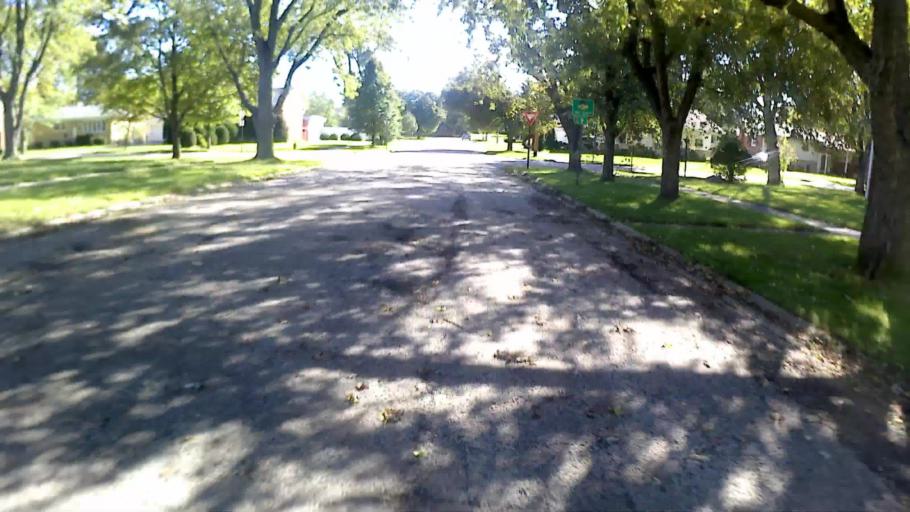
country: US
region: Illinois
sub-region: DuPage County
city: Wood Dale
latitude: 41.9556
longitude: -87.9960
